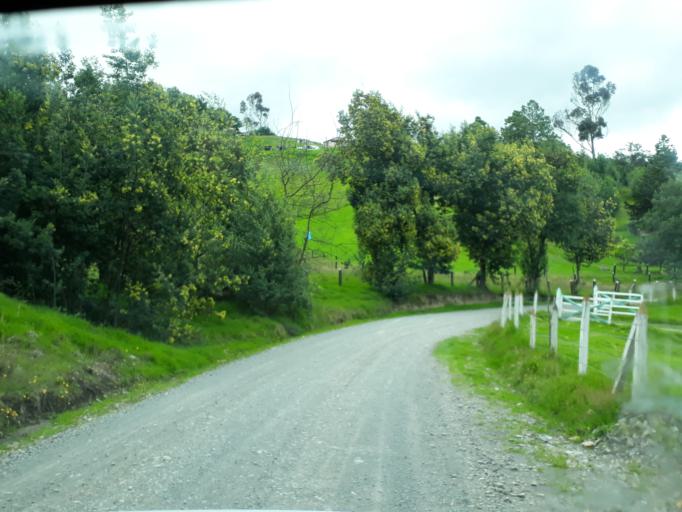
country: CO
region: Cundinamarca
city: La Mesa
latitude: 5.2910
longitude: -73.9056
